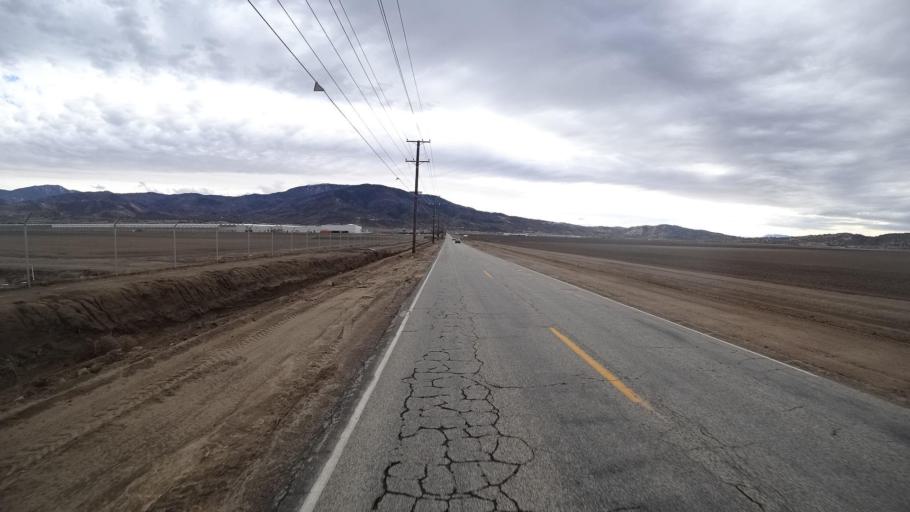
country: US
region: California
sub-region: Kern County
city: Bear Valley Springs
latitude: 35.1207
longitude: -118.6017
